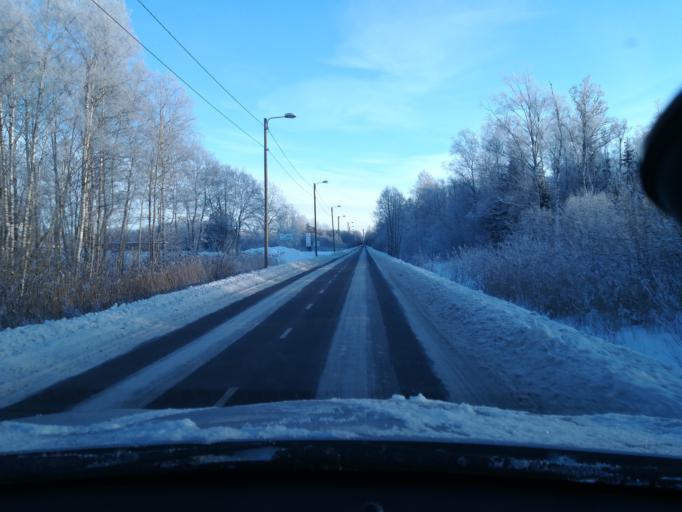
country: EE
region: Harju
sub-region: Saue vald
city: Laagri
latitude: 59.3926
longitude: 24.6052
